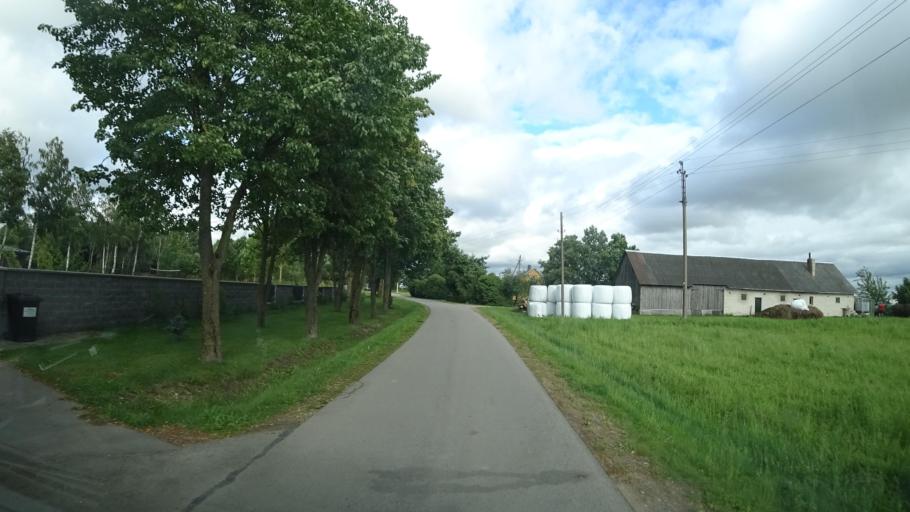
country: LT
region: Marijampoles apskritis
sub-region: Marijampole Municipality
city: Marijampole
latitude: 54.5188
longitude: 23.3324
